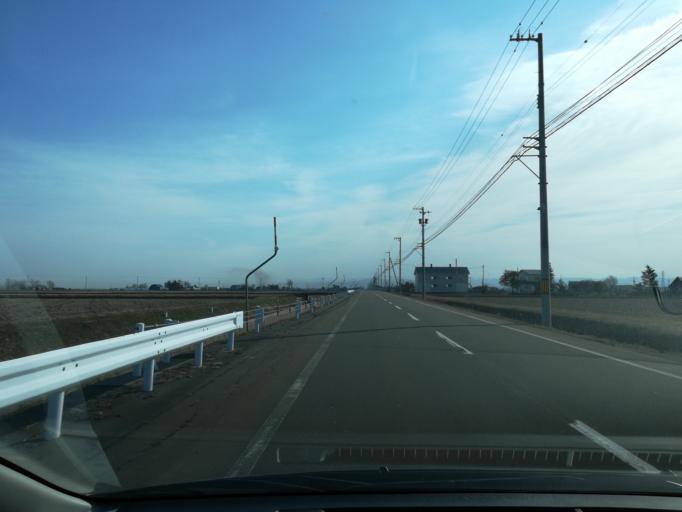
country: JP
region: Hokkaido
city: Iwamizawa
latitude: 43.1727
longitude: 141.6727
